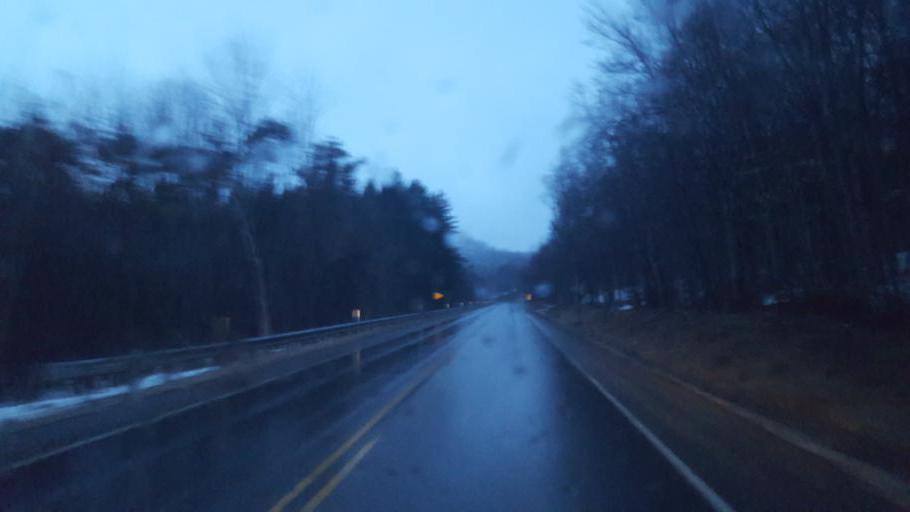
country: US
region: Pennsylvania
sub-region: McKean County
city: Smethport
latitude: 41.8235
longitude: -78.3767
